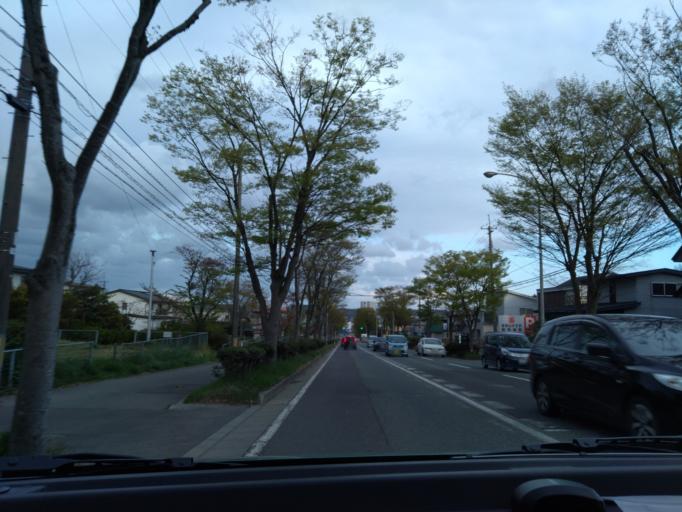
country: JP
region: Akita
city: Akita
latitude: 39.7330
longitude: 140.1415
